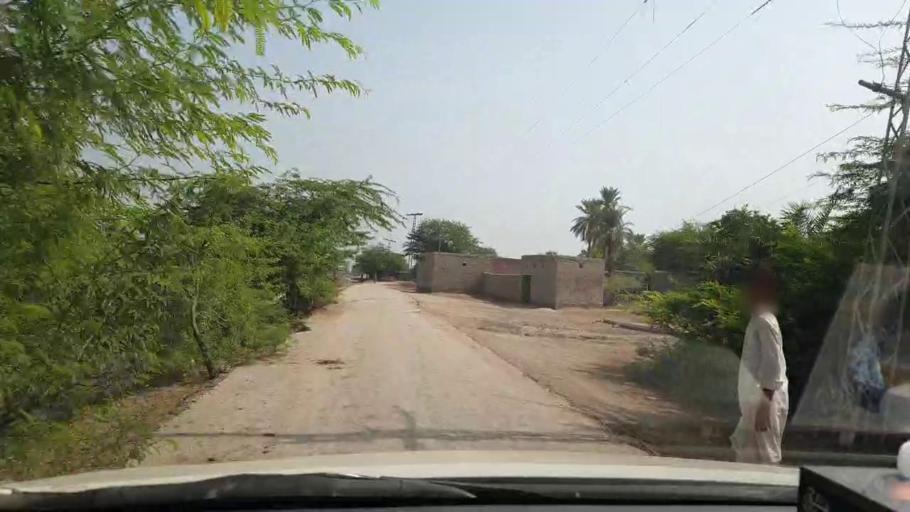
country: PK
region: Sindh
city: Shikarpur
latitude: 27.9819
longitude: 68.6659
